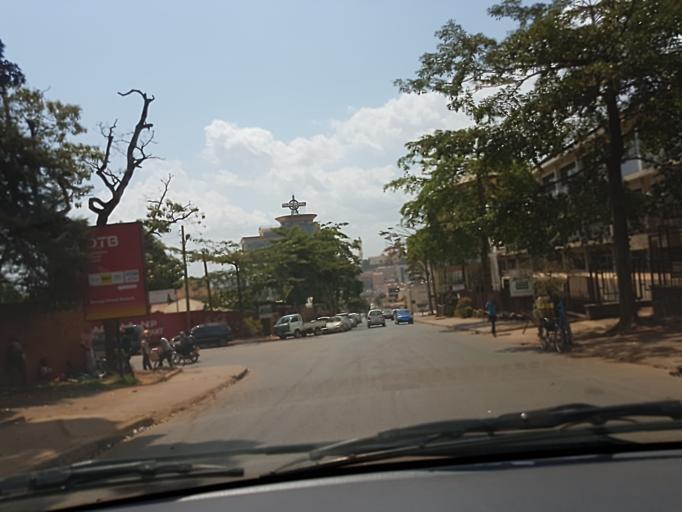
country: UG
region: Central Region
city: Kampala Central Division
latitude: 0.3192
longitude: 32.5765
